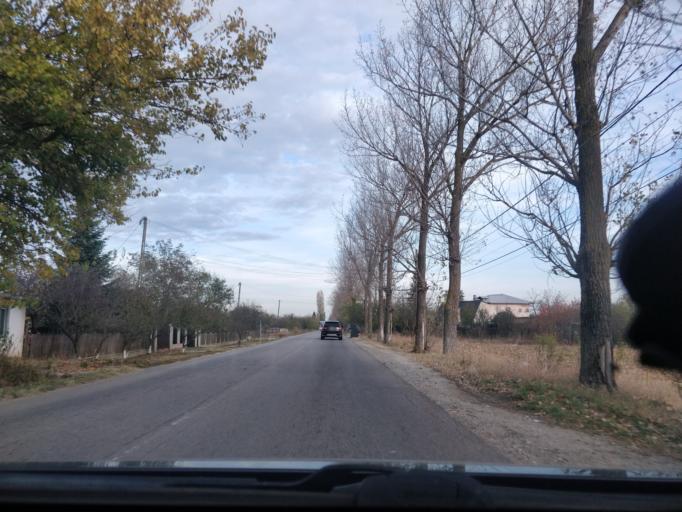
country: RO
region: Giurgiu
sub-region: Comuna Crevedia Mare
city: Crevedia Mare
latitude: 44.4308
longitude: 25.6382
